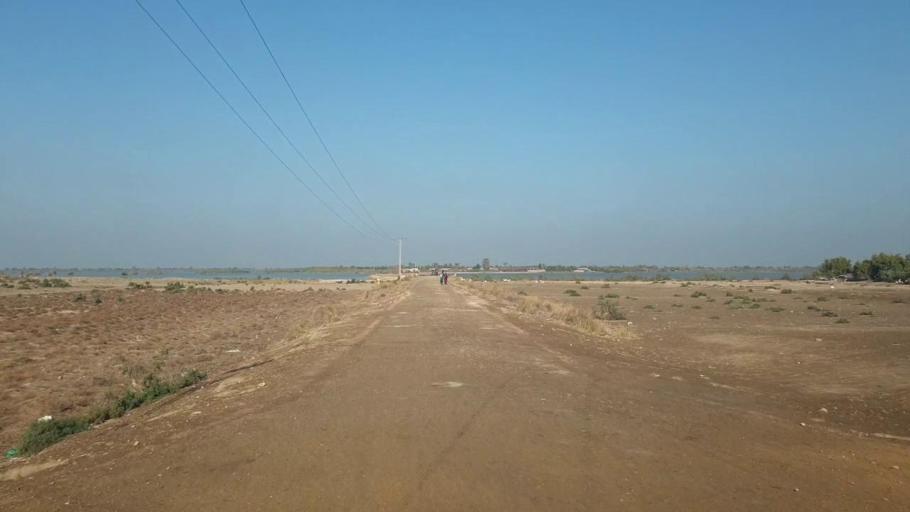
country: PK
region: Sindh
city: Shahdadpur
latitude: 25.8956
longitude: 68.5843
